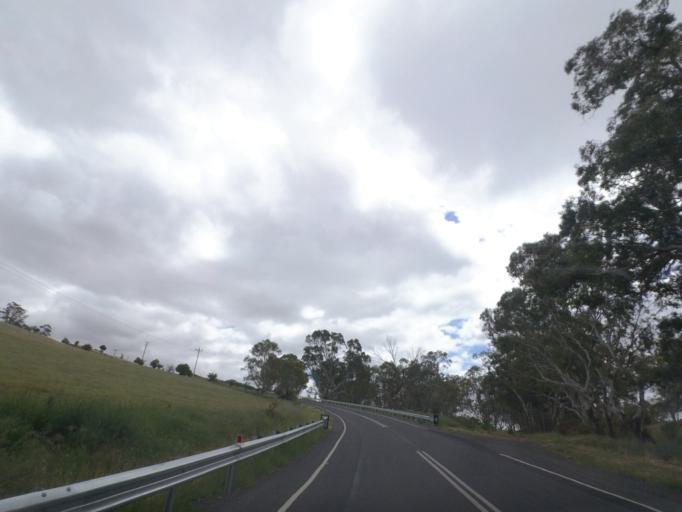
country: AU
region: Victoria
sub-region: Whittlesea
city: Whittlesea
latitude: -37.1901
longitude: 145.0388
